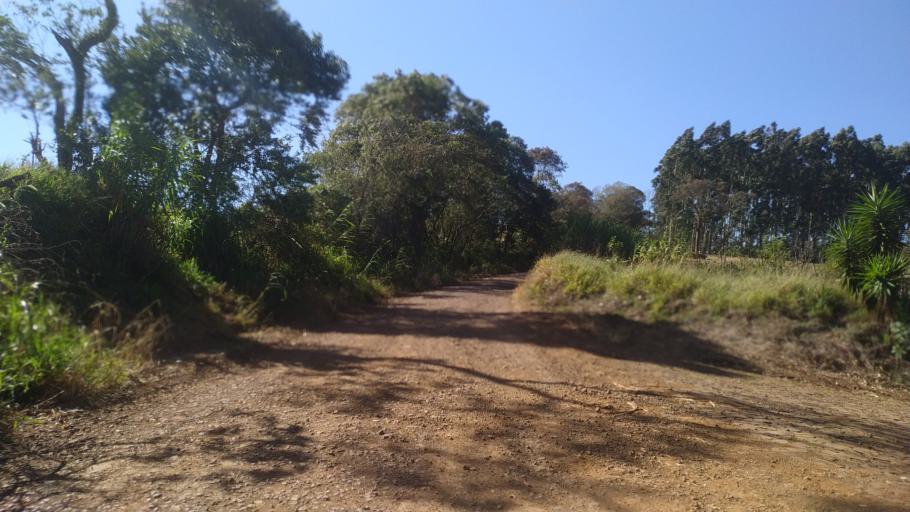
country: BR
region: Santa Catarina
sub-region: Chapeco
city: Chapeco
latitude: -27.1489
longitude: -52.6106
